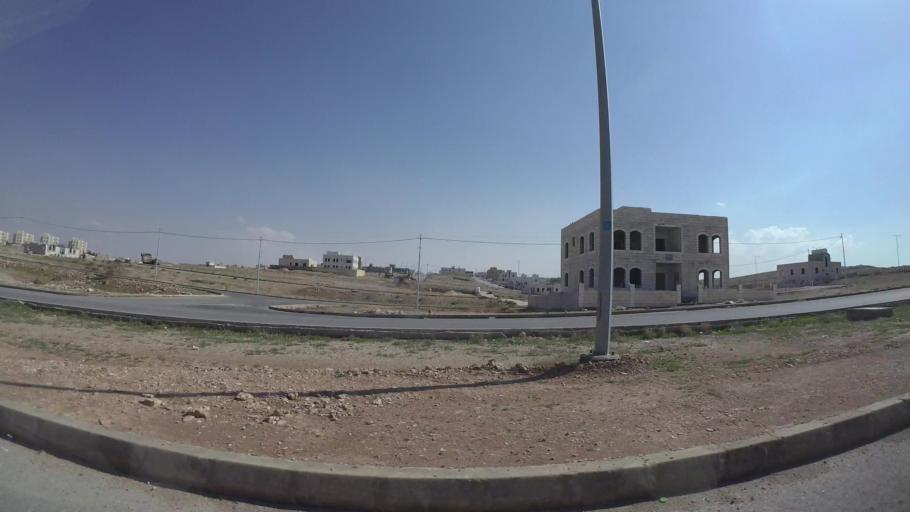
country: JO
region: Zarqa
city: Zarqa
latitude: 32.0545
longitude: 36.1146
